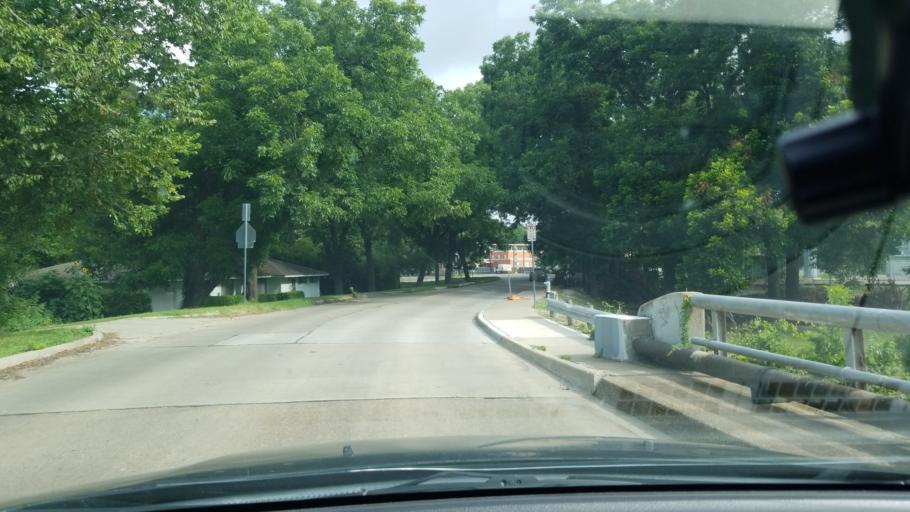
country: US
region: Texas
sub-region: Dallas County
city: Highland Park
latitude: 32.8111
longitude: -96.7089
